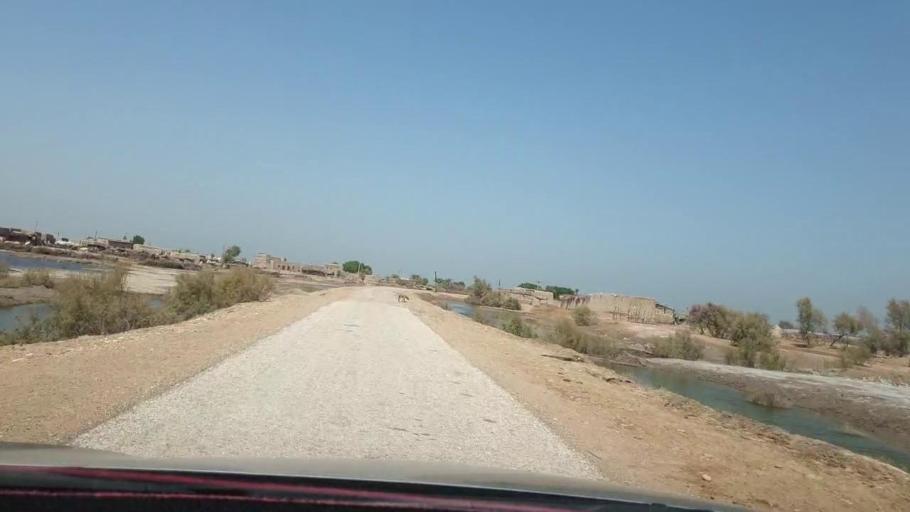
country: PK
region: Sindh
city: Warah
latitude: 27.5751
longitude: 67.7569
